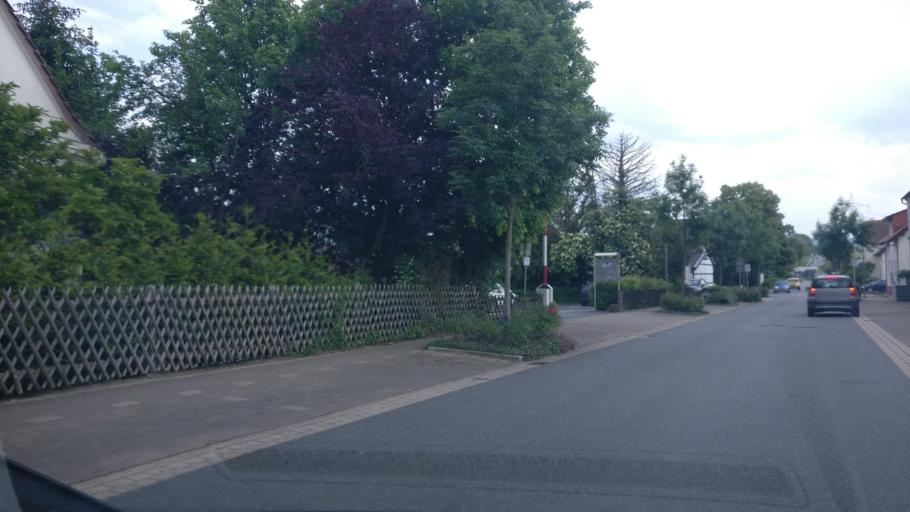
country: DE
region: North Rhine-Westphalia
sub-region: Regierungsbezirk Detmold
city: Leopoldshohe
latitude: 52.0112
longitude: 8.6989
